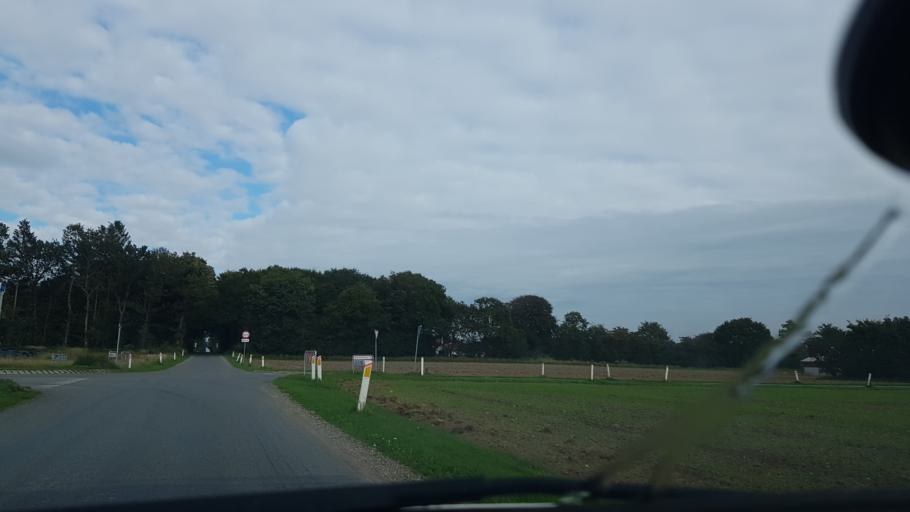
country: DK
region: South Denmark
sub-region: Vejen Kommune
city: Brorup
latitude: 55.4792
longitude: 8.9782
